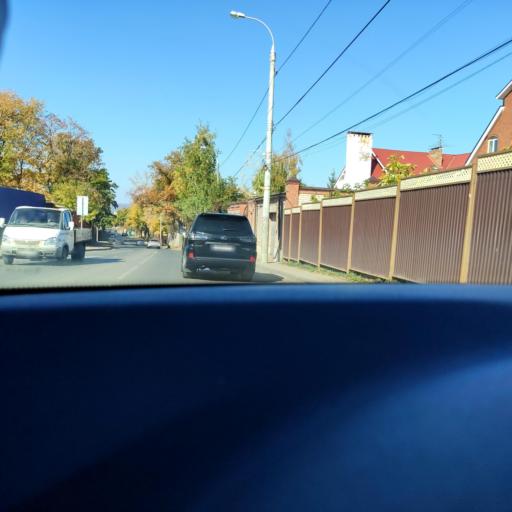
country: RU
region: Samara
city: Samara
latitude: 53.2708
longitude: 50.1955
